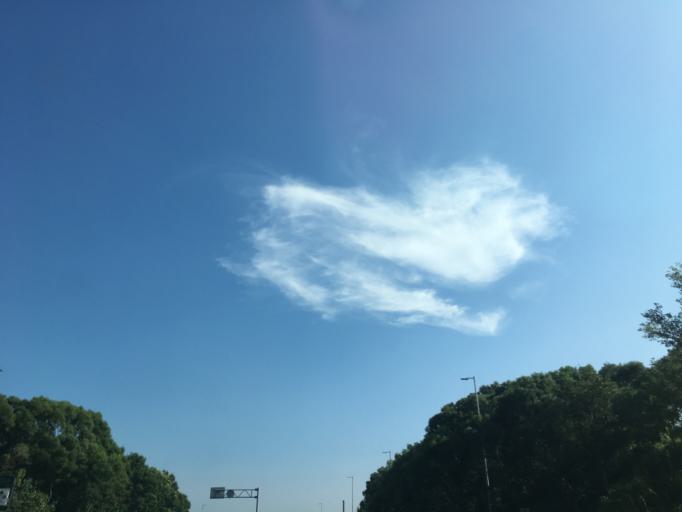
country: TW
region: Taiwan
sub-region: Hsinchu
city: Hsinchu
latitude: 24.7866
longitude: 120.9492
